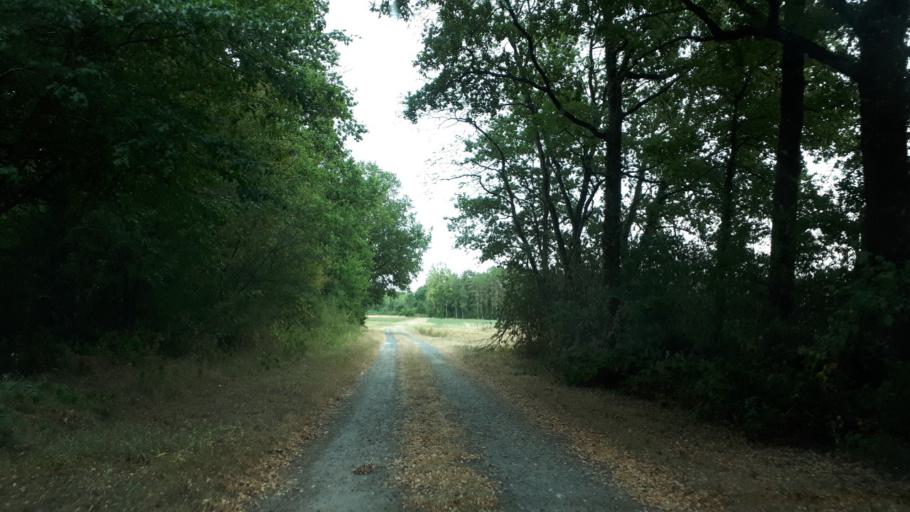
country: FR
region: Centre
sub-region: Departement du Loir-et-Cher
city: Saint-Romain-sur-Cher
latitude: 47.3534
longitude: 1.3942
